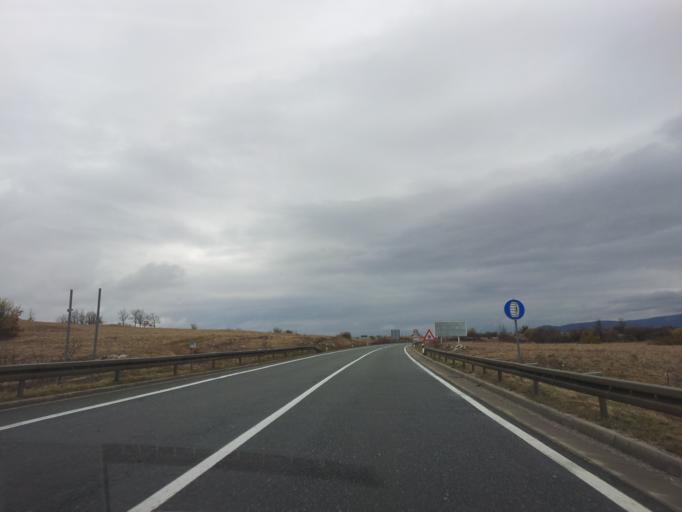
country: HR
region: Zadarska
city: Gracac
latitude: 44.5119
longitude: 15.7450
